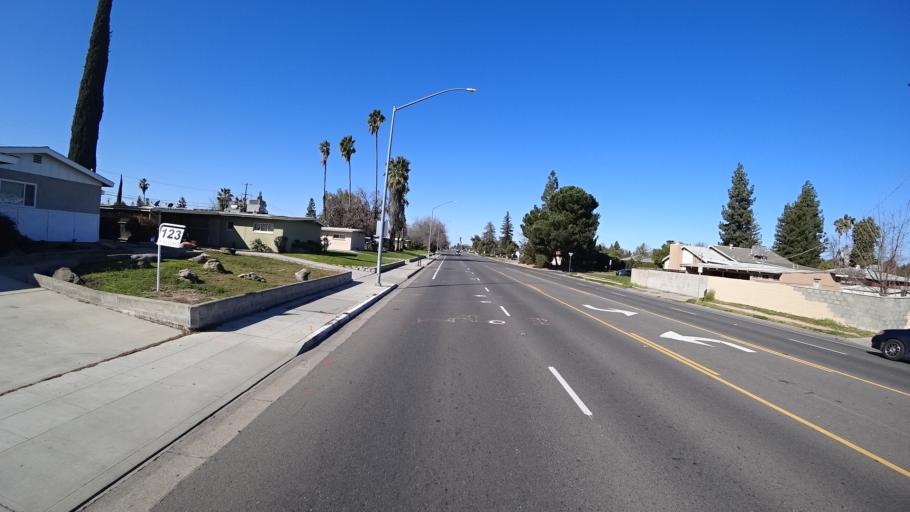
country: US
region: California
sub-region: Fresno County
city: Fresno
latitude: 36.8229
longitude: -119.7931
